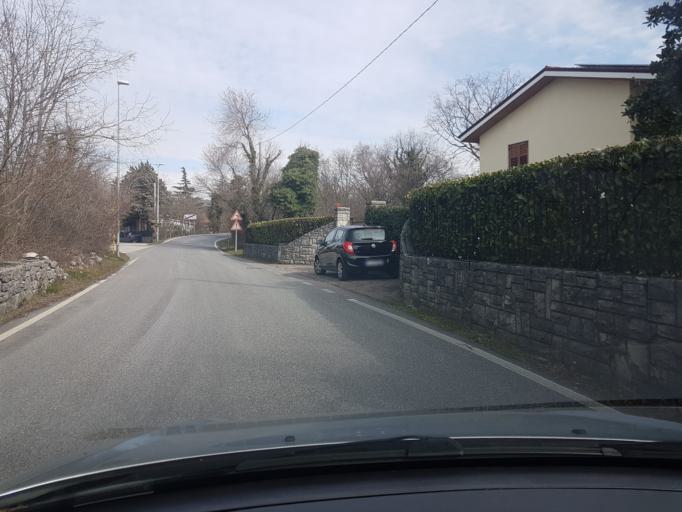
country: IT
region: Friuli Venezia Giulia
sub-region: Provincia di Trieste
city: Aurisina Cave
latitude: 45.7603
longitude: 13.6615
